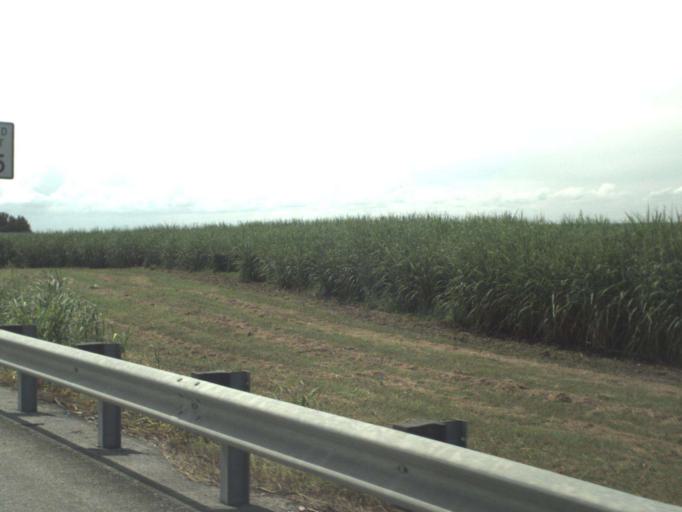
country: US
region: Florida
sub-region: Palm Beach County
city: Pahokee
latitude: 26.8044
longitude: -80.6534
